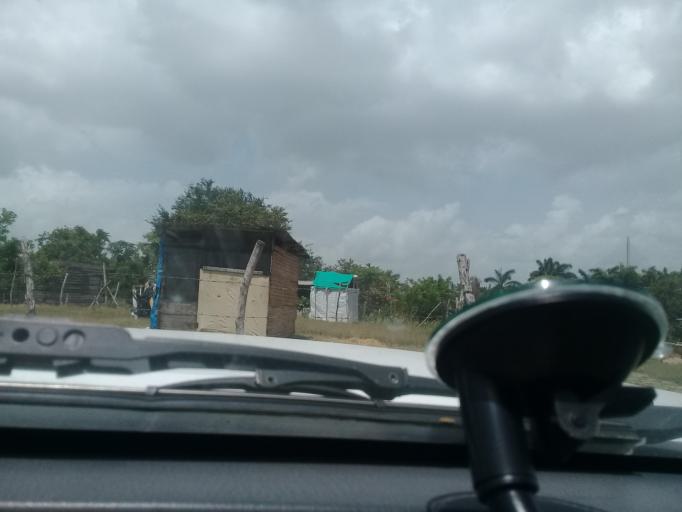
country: MX
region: Veracruz
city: Anahuac
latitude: 22.2256
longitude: -97.8264
